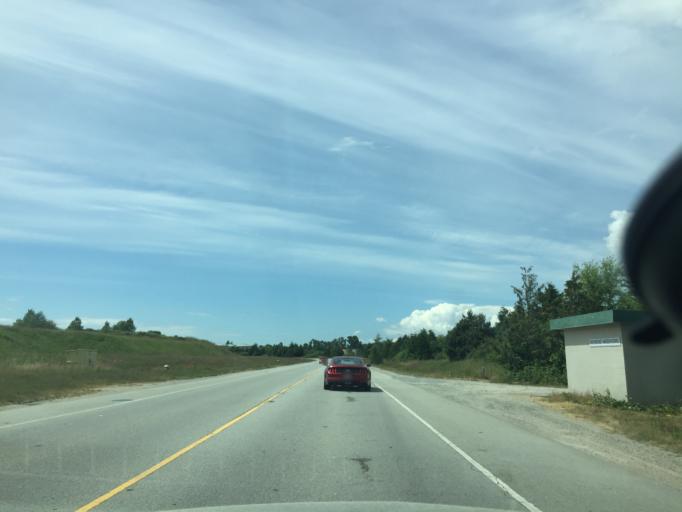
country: CA
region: British Columbia
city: Richmond
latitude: 49.2031
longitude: -123.1520
